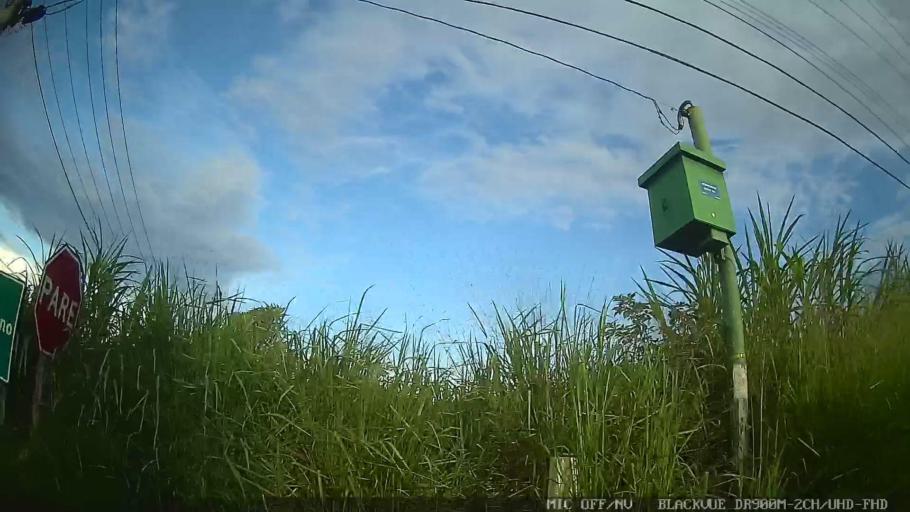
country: BR
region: Sao Paulo
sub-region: Mogi das Cruzes
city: Mogi das Cruzes
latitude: -23.5406
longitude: -46.1573
